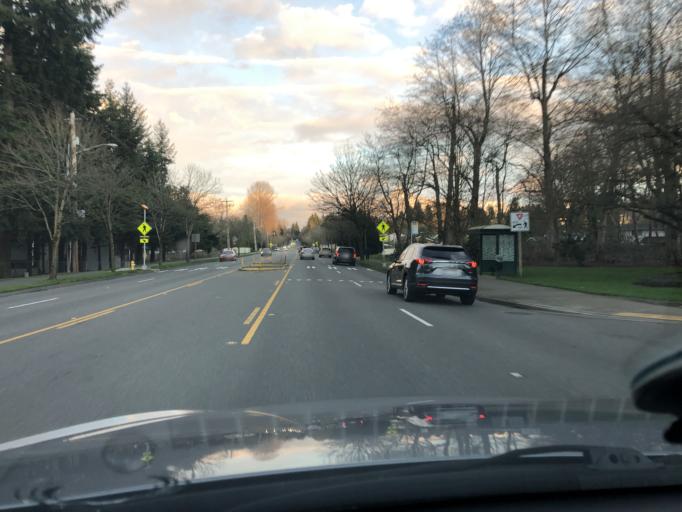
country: US
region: Washington
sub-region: King County
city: Federal Way
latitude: 47.3152
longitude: -122.3576
